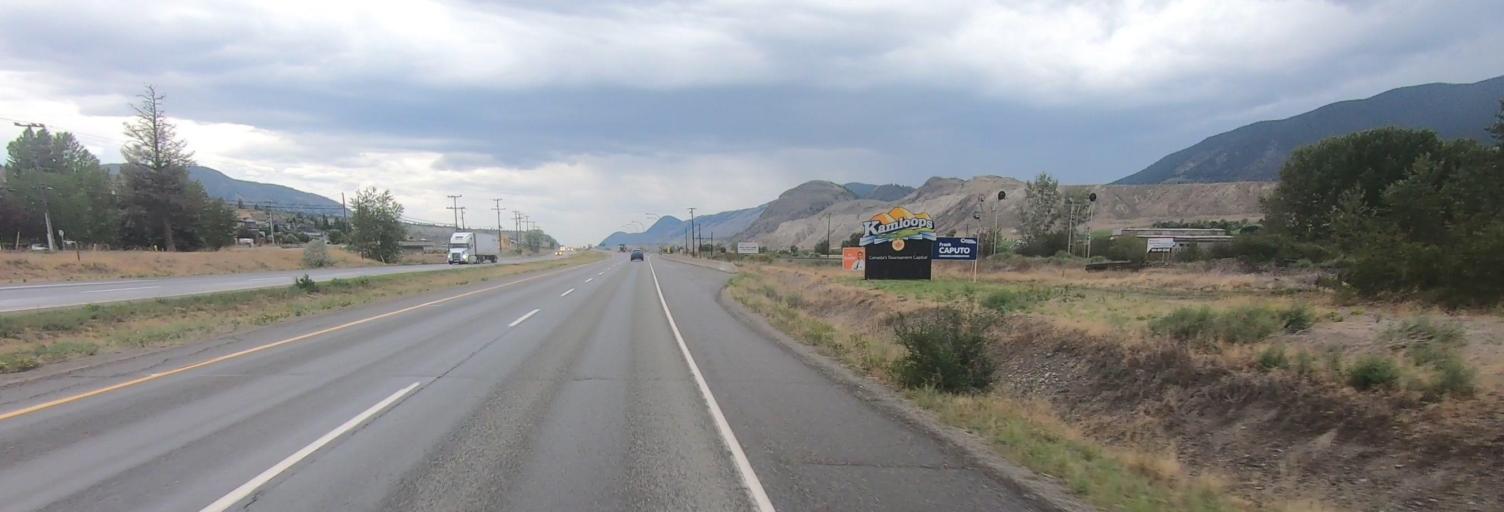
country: CA
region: British Columbia
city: Kamloops
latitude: 50.6557
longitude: -120.0786
